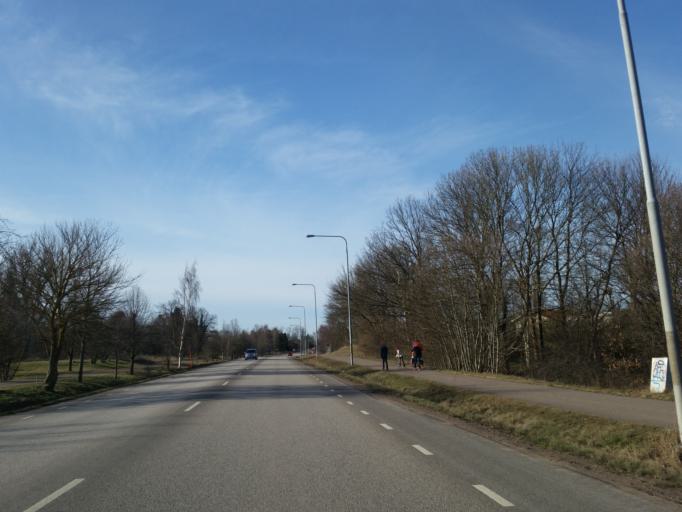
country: SE
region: Kalmar
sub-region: Kalmar Kommun
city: Kalmar
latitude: 56.6969
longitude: 16.3304
